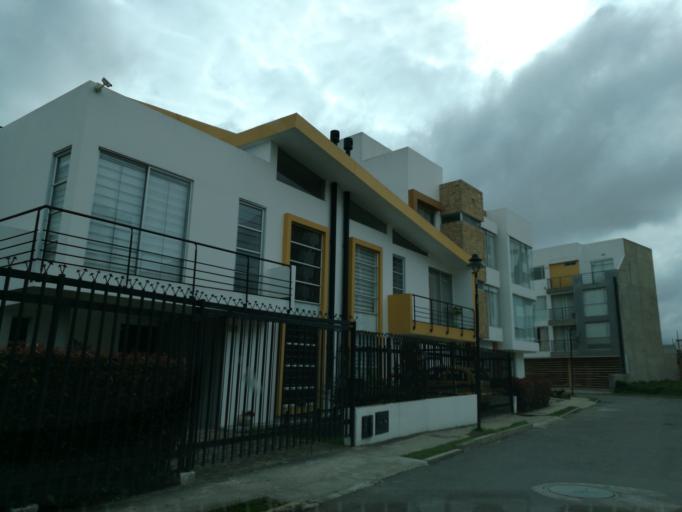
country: CO
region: Boyaca
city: Tunja
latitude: 5.5506
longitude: -73.3594
